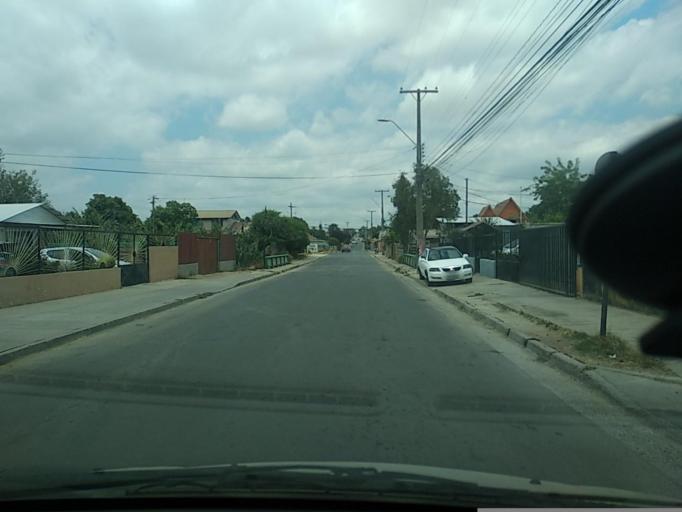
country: CL
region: Valparaiso
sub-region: Provincia de Marga Marga
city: Villa Alemana
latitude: -33.0396
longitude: -71.4077
